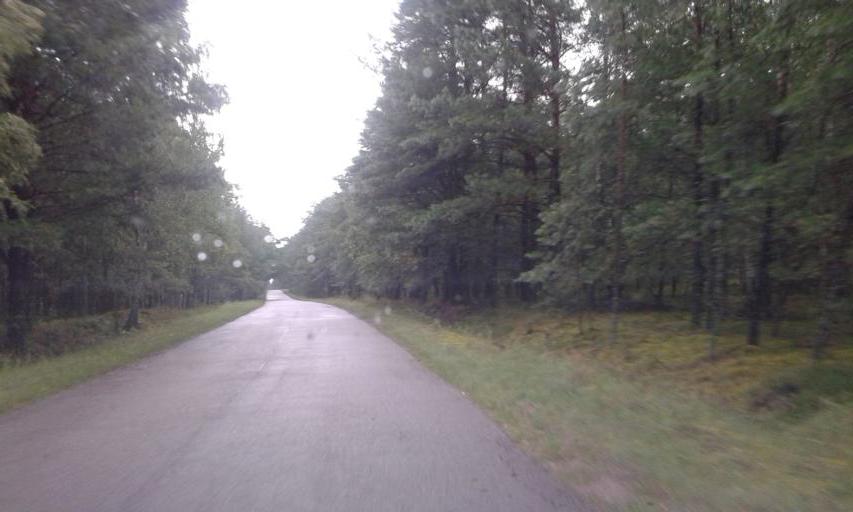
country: PL
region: West Pomeranian Voivodeship
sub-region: Powiat szczecinecki
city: Borne Sulinowo
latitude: 53.5429
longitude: 16.5113
